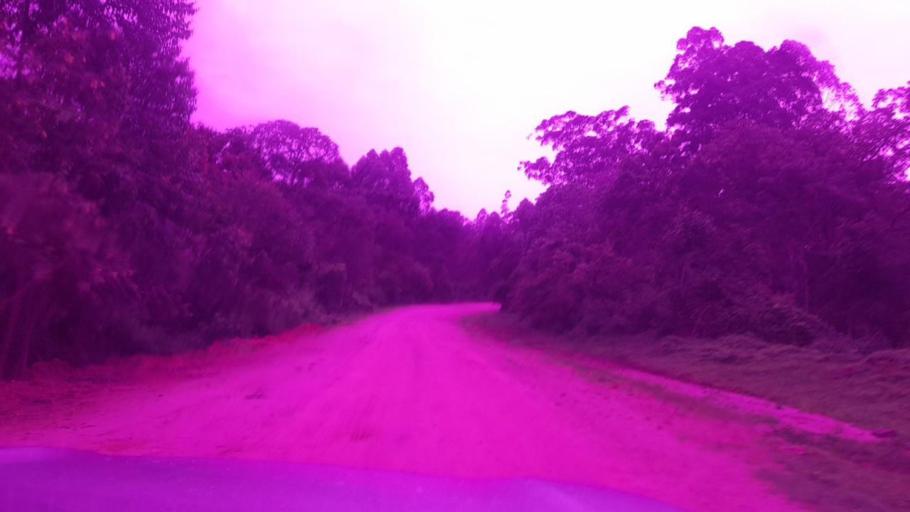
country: ET
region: Southern Nations, Nationalities, and People's Region
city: Bonga
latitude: 7.4431
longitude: 36.1475
